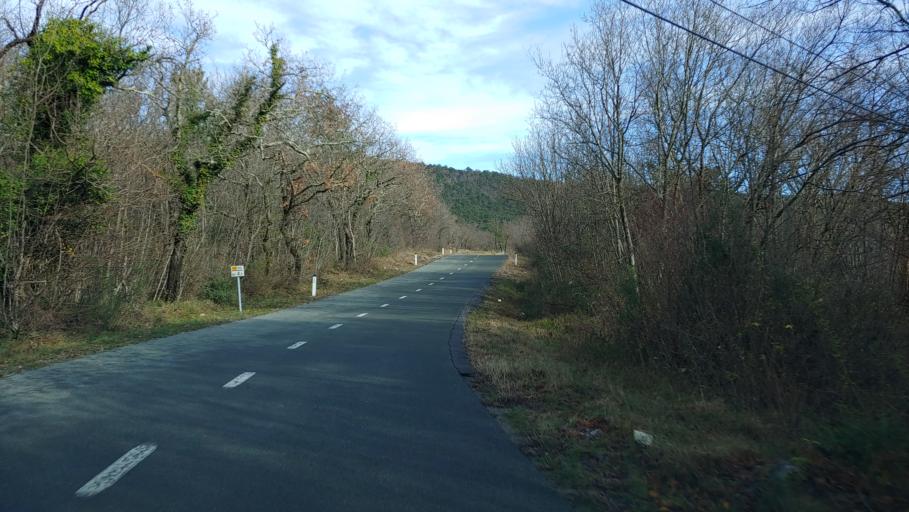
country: IT
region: Friuli Venezia Giulia
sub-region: Provincia di Trieste
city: Sistiana-Visogliano
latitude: 45.8122
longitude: 13.6610
